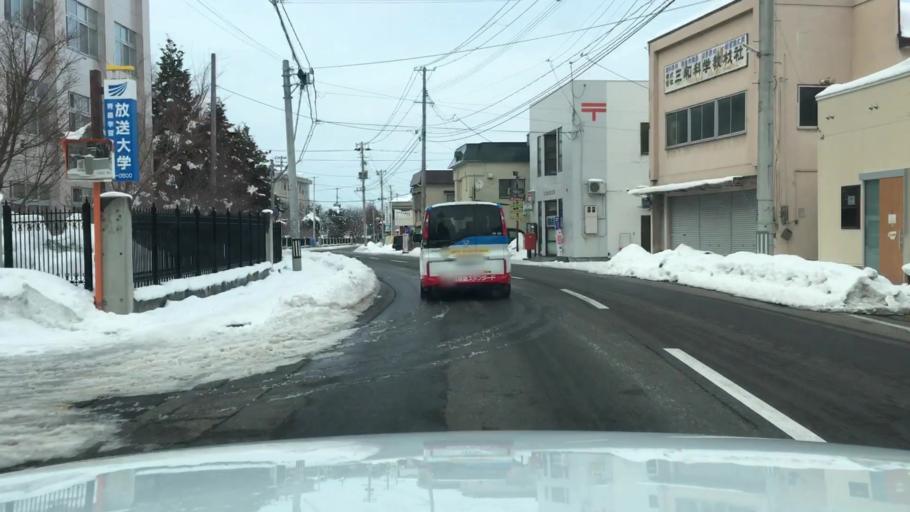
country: JP
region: Aomori
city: Hirosaki
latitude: 40.5876
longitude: 140.4746
